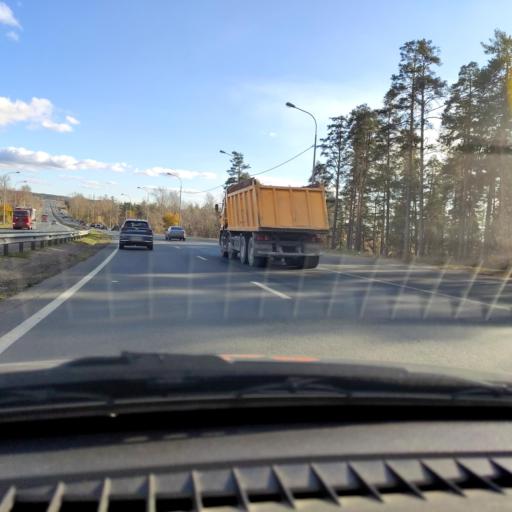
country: RU
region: Samara
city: Zhigulevsk
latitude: 53.5328
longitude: 49.5169
